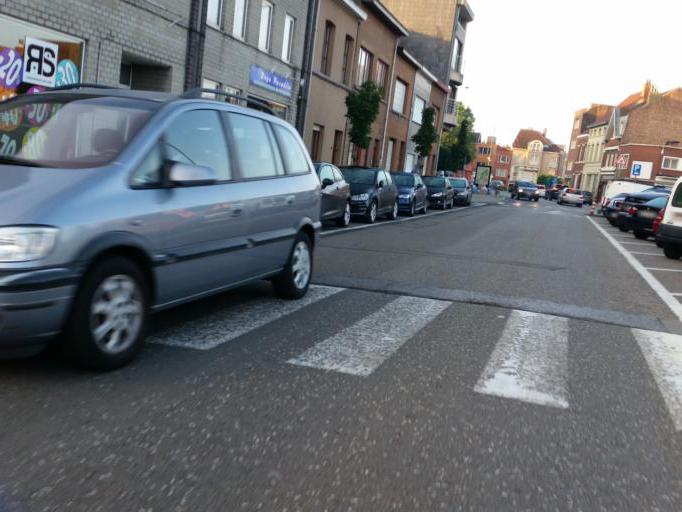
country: BE
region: Flanders
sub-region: Provincie Vlaams-Brabant
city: Vilvoorde
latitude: 50.9321
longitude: 4.4241
